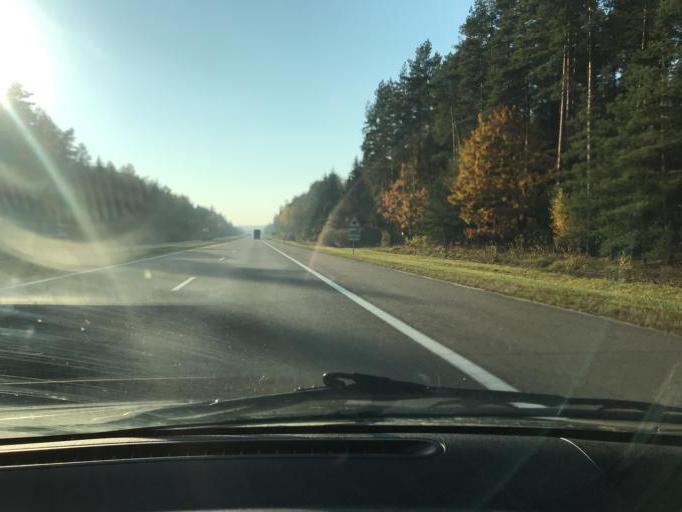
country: BY
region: Minsk
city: Krupki
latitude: 54.3071
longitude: 28.9992
